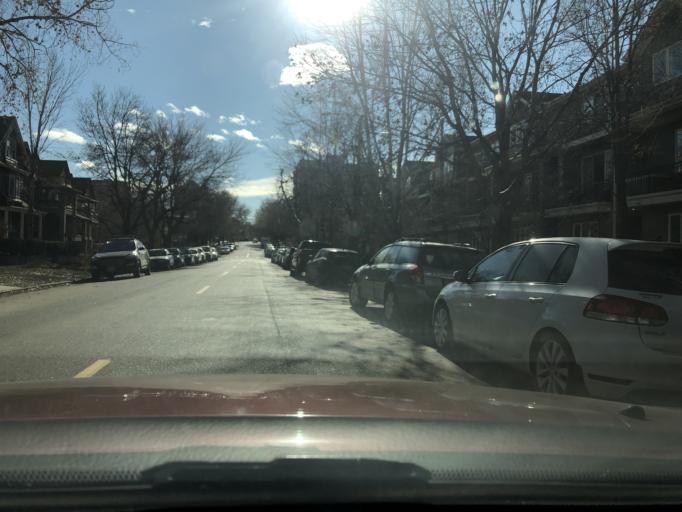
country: US
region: Colorado
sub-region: Denver County
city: Denver
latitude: 39.7425
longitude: -104.9685
